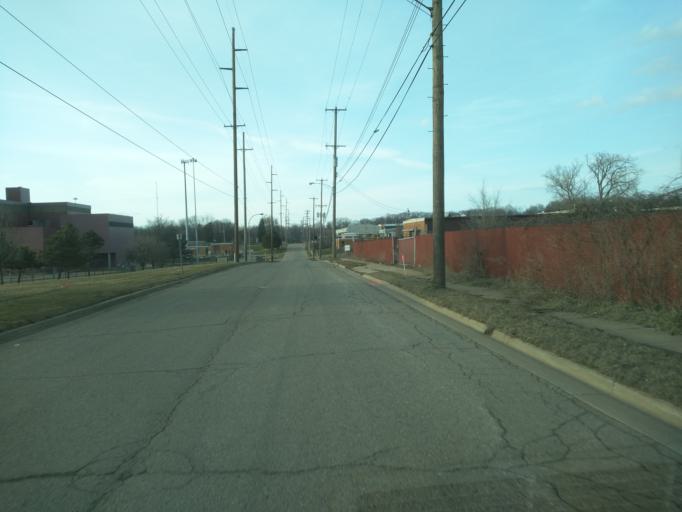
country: US
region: Michigan
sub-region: Ingham County
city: Edgemont Park
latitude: 42.7514
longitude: -84.5793
